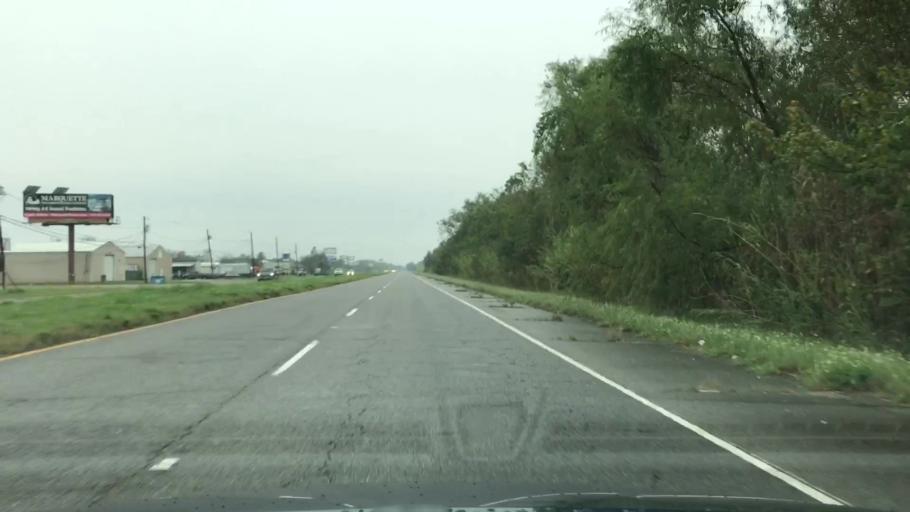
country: US
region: Louisiana
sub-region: Saint Charles Parish
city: Des Allemands
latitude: 29.8090
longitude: -90.4948
